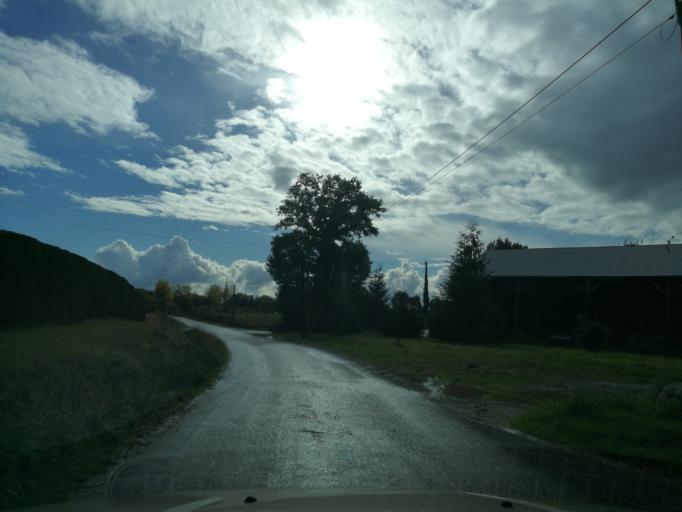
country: FR
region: Brittany
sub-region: Departement d'Ille-et-Vilaine
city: Pleumeleuc
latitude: 48.2074
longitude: -1.9349
